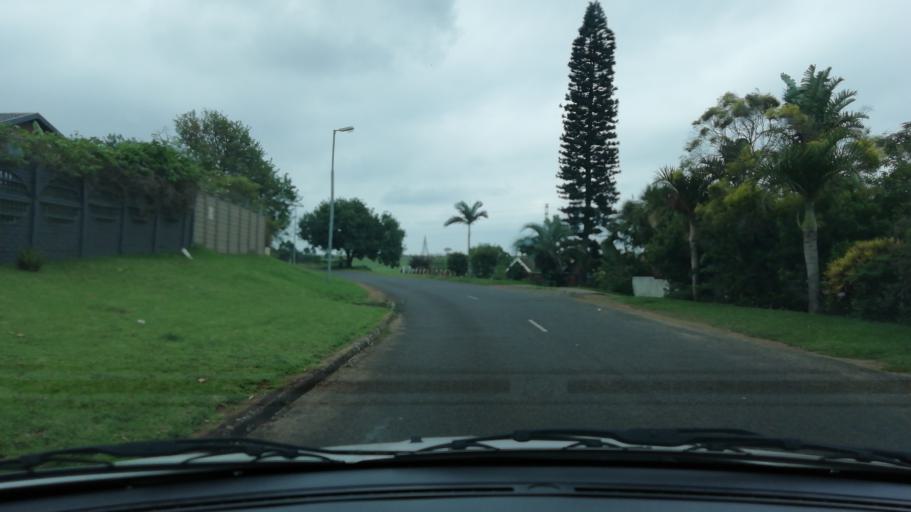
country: ZA
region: KwaZulu-Natal
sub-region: uThungulu District Municipality
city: Empangeni
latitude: -28.7361
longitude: 31.9026
